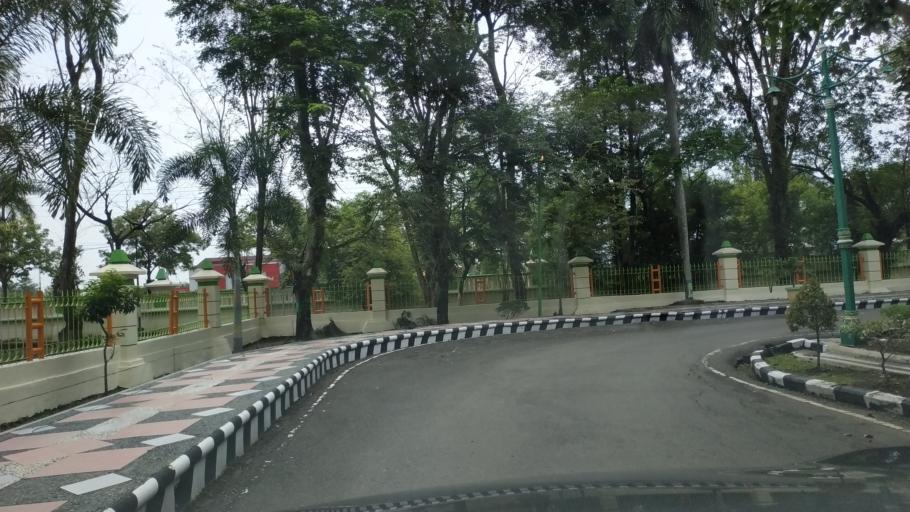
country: ID
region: Central Java
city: Slawi
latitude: -6.9943
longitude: 109.1273
